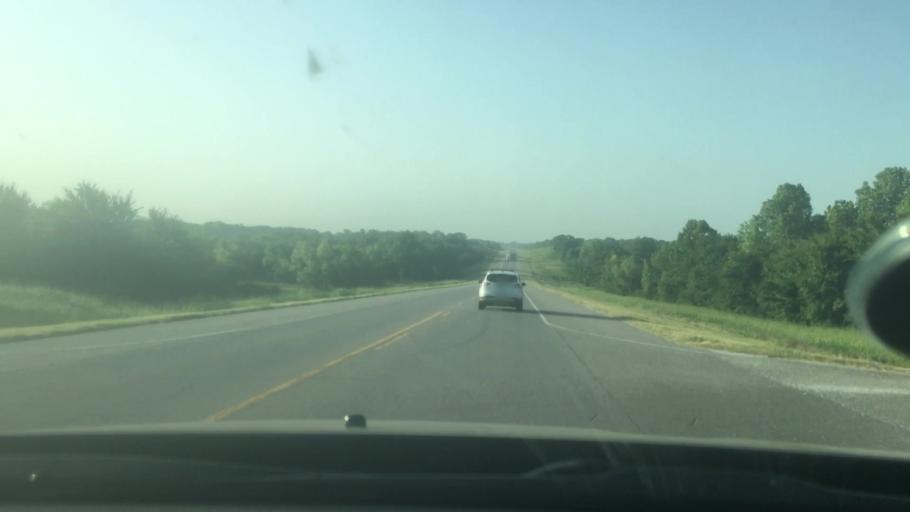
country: US
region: Oklahoma
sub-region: Pontotoc County
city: Ada
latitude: 34.6657
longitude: -96.5654
